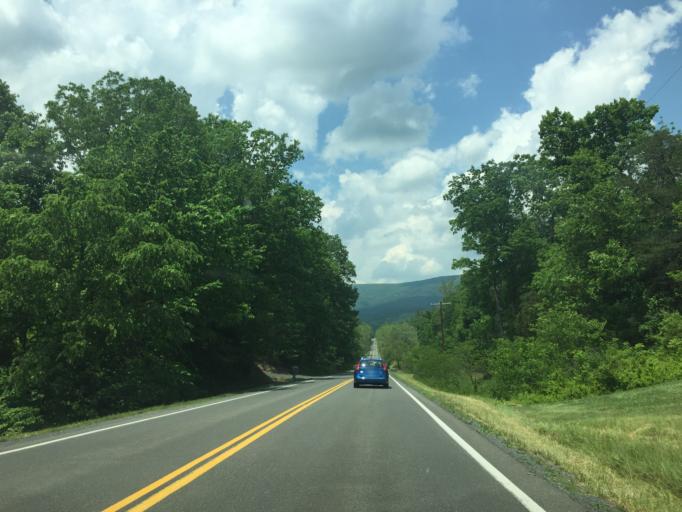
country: US
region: Virginia
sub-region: Shenandoah County
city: Strasburg
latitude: 39.0792
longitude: -78.4216
